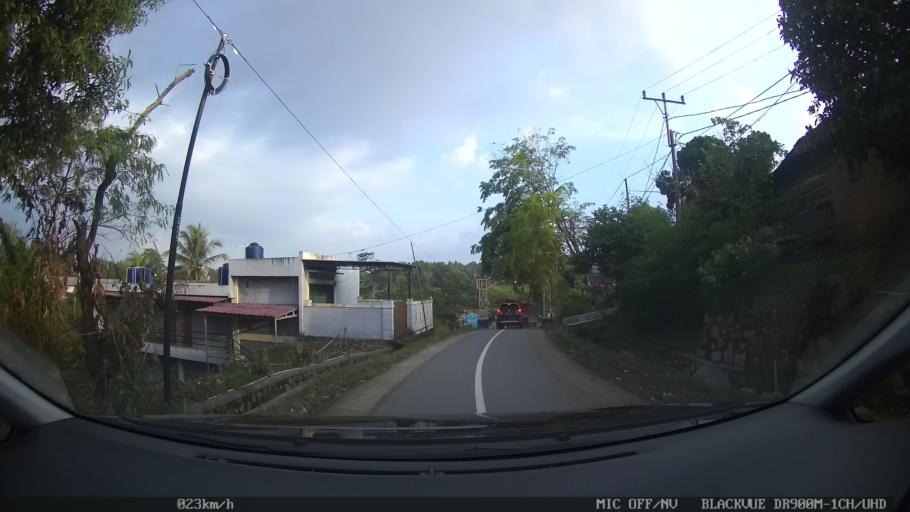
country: ID
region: Lampung
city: Panjang
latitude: -5.4030
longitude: 105.3503
